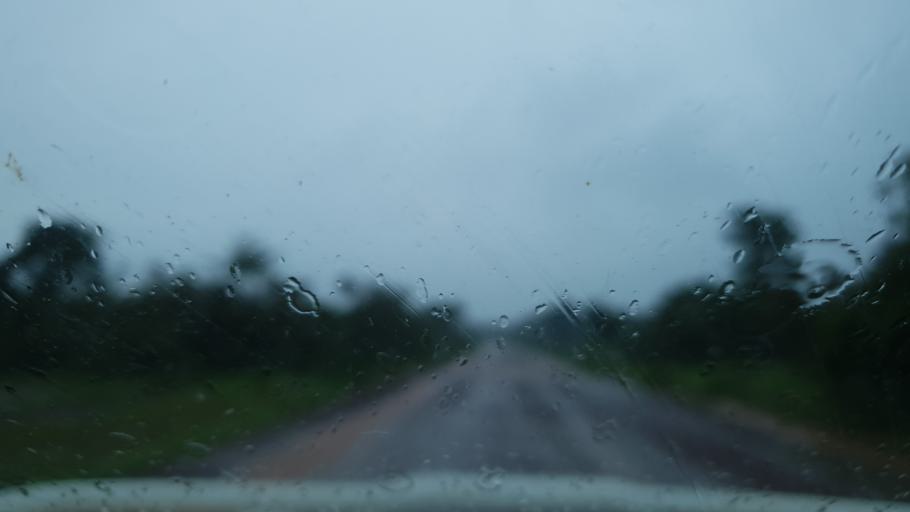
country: ML
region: Sikasso
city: Kolondieba
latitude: 11.6154
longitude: -6.6771
